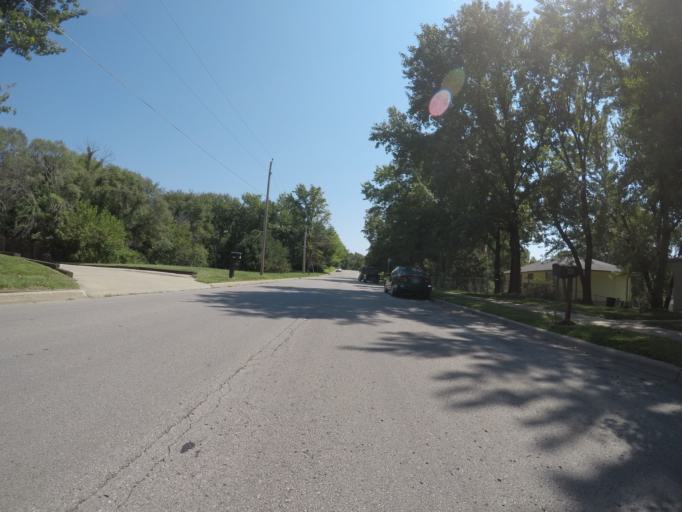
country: US
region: Kansas
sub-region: Leavenworth County
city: Leavenworth
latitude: 39.2948
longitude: -94.9008
